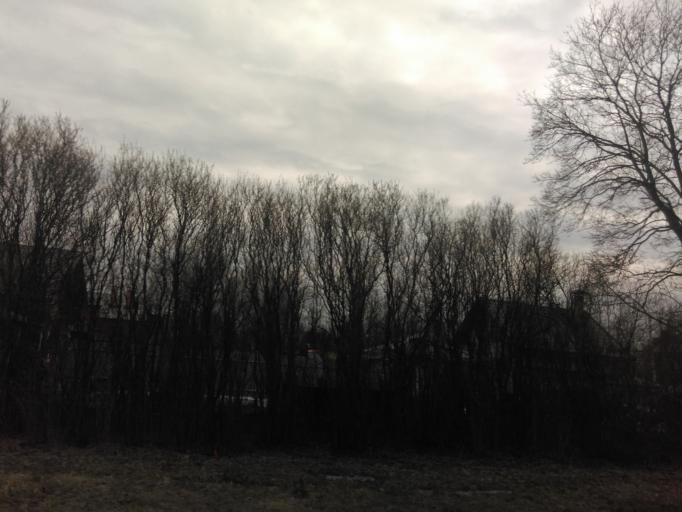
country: RU
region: Moskovskaya
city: Nikolina Gora
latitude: 55.7386
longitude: 36.9827
